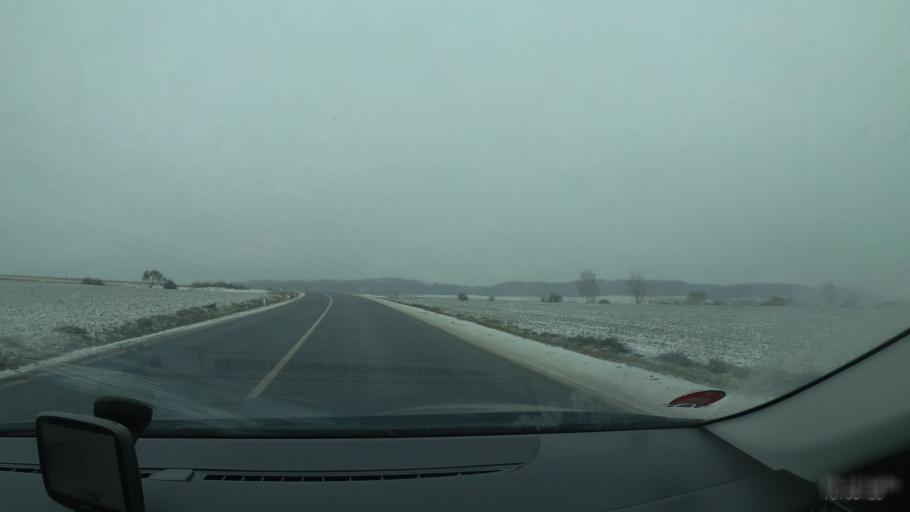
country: CZ
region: Central Bohemia
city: Revnicov
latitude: 50.1805
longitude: 13.8159
